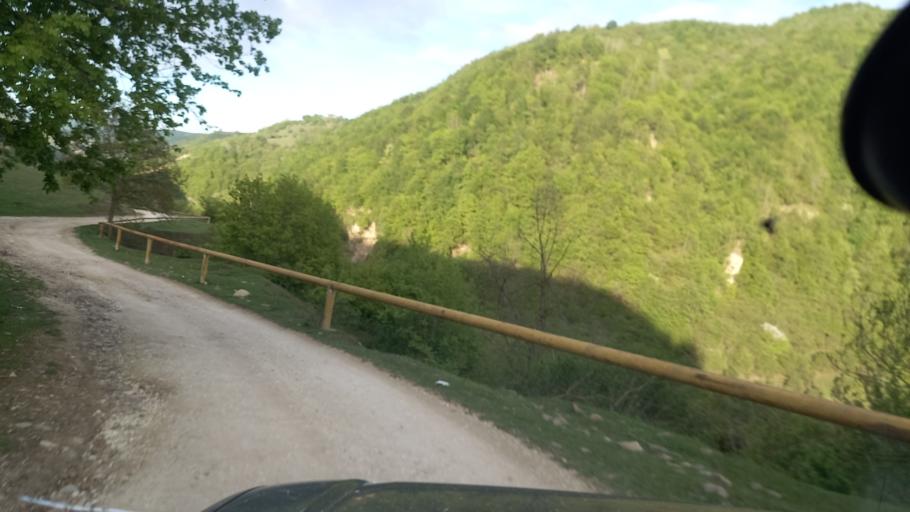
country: RU
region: Dagestan
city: Khuchni
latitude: 41.9487
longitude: 47.8368
